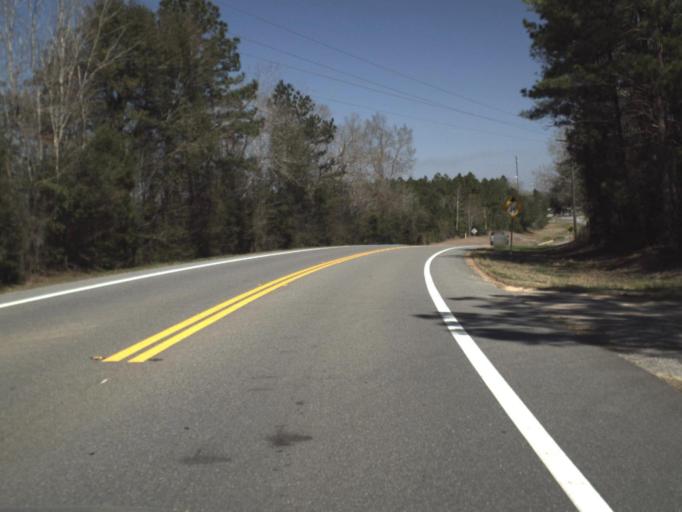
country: US
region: Florida
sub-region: Jackson County
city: Sneads
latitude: 30.6501
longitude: -85.0394
